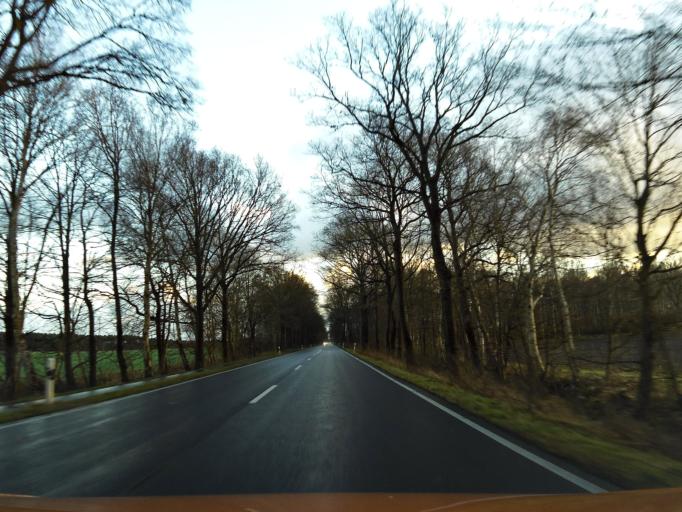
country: DE
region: Lower Saxony
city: Meinersen
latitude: 52.4326
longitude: 10.3333
